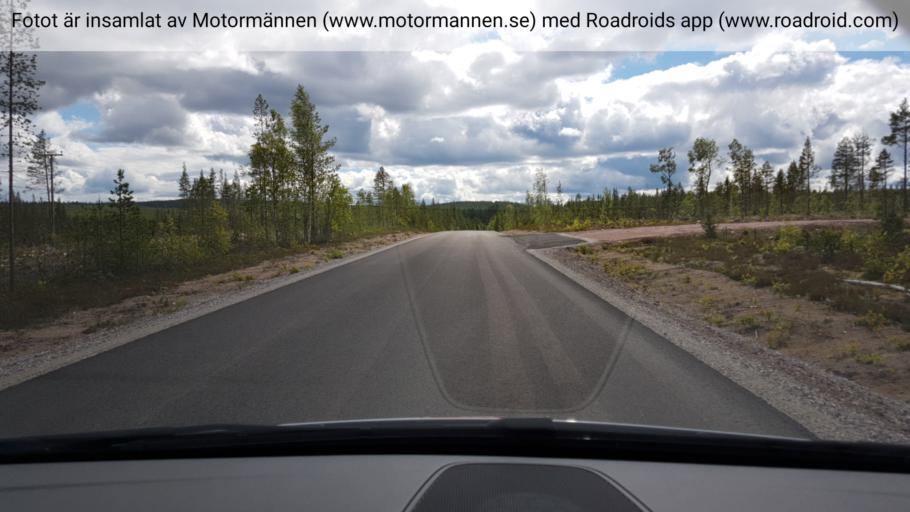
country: SE
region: Jaemtland
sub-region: Harjedalens Kommun
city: Sveg
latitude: 61.6903
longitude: 14.1865
